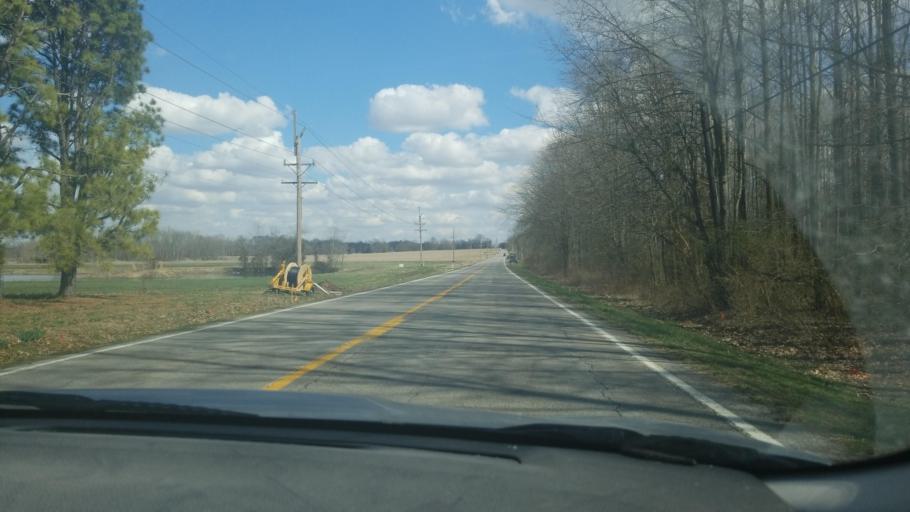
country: US
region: Illinois
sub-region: Saline County
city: Harrisburg
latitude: 37.7388
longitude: -88.5882
